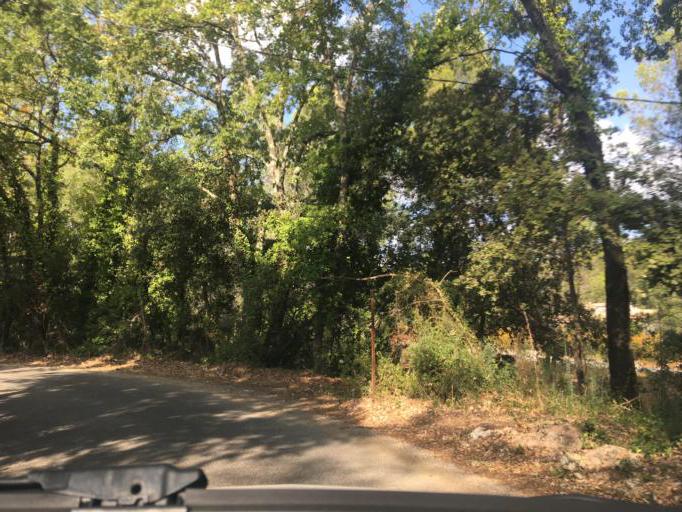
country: FR
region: Provence-Alpes-Cote d'Azur
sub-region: Departement du Var
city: Lorgues
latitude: 43.4930
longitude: 6.3950
